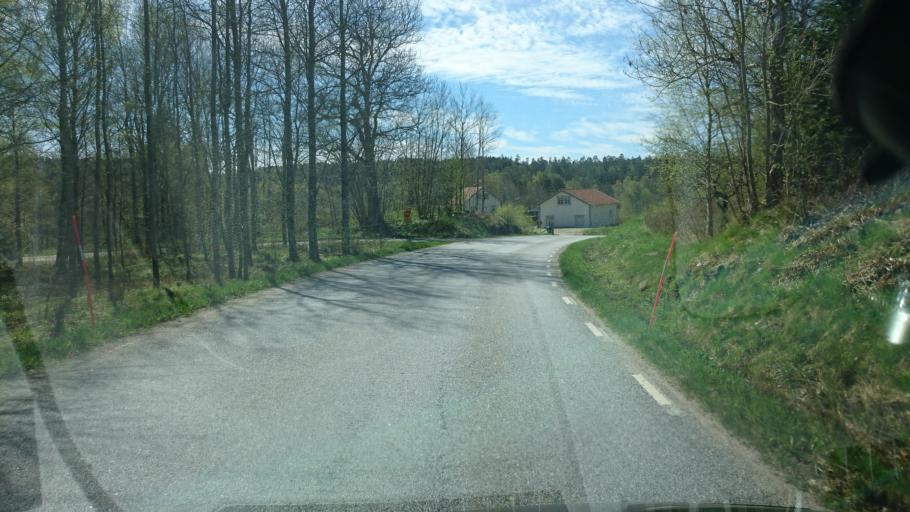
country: SE
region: Vaestra Goetaland
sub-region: Munkedals Kommun
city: Munkedal
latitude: 58.4166
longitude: 11.6852
